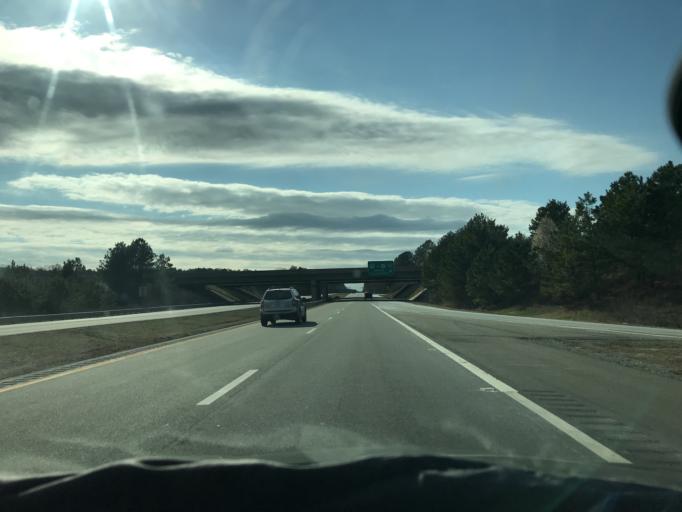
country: US
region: Virginia
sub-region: Chesterfield County
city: Brandermill
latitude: 37.4617
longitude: -77.6359
